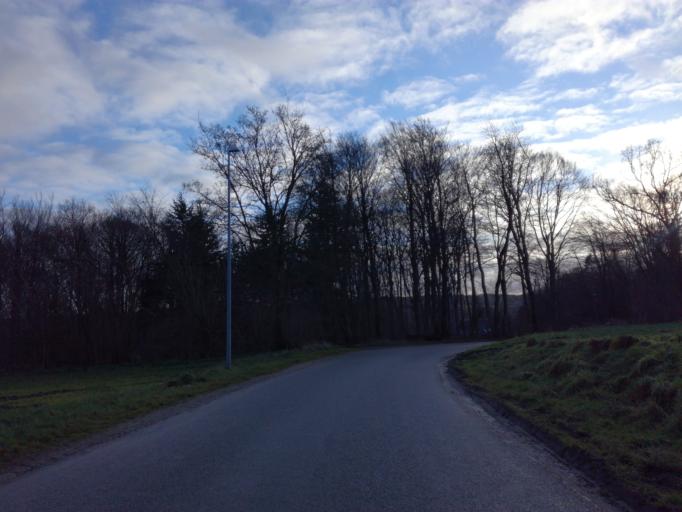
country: DK
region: South Denmark
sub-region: Fredericia Kommune
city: Taulov
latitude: 55.5526
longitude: 9.6026
